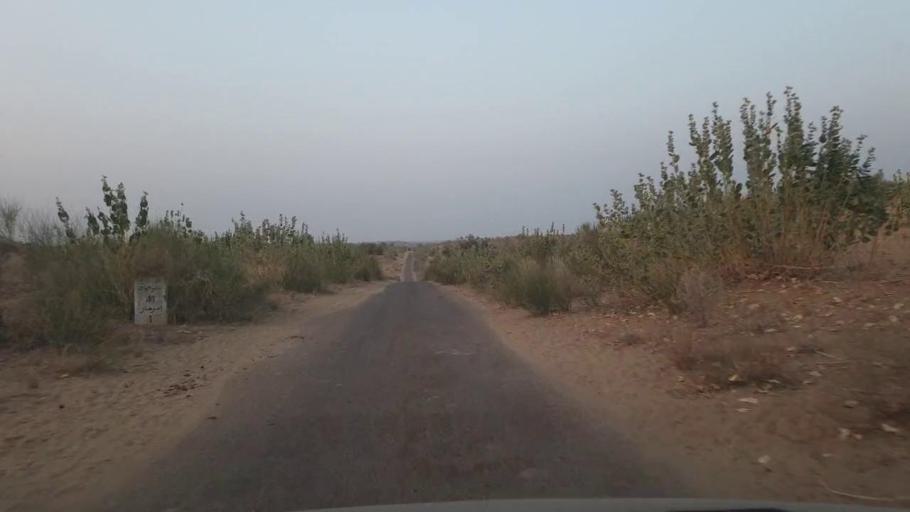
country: PK
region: Sindh
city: Umarkot
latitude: 25.3202
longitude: 70.0575
